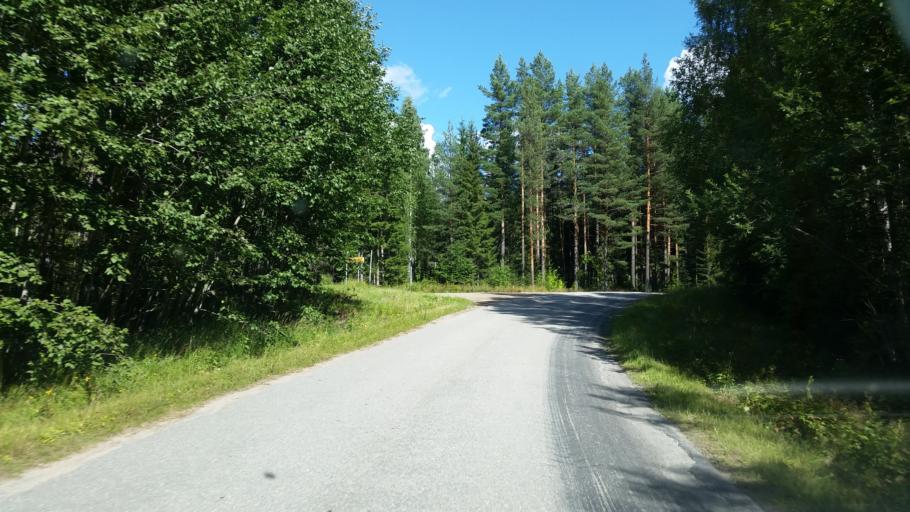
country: SE
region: Gaevleborg
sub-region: Ljusdals Kommun
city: Ljusdal
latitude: 61.9665
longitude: 16.3175
